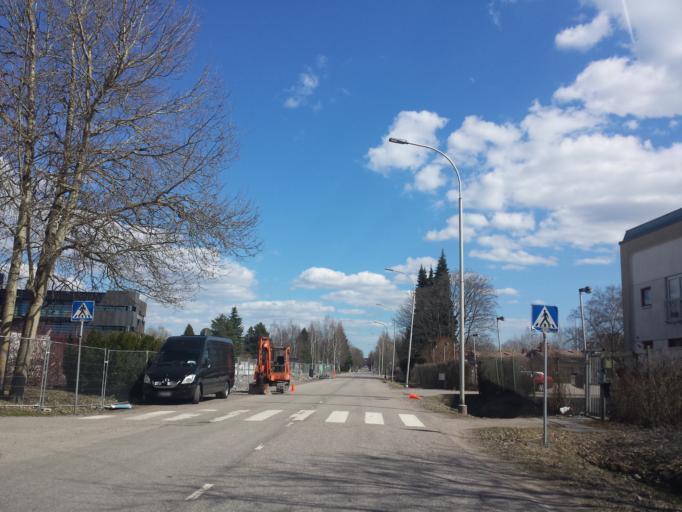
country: FI
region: Uusimaa
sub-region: Helsinki
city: Vantaa
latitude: 60.2941
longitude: 25.0086
